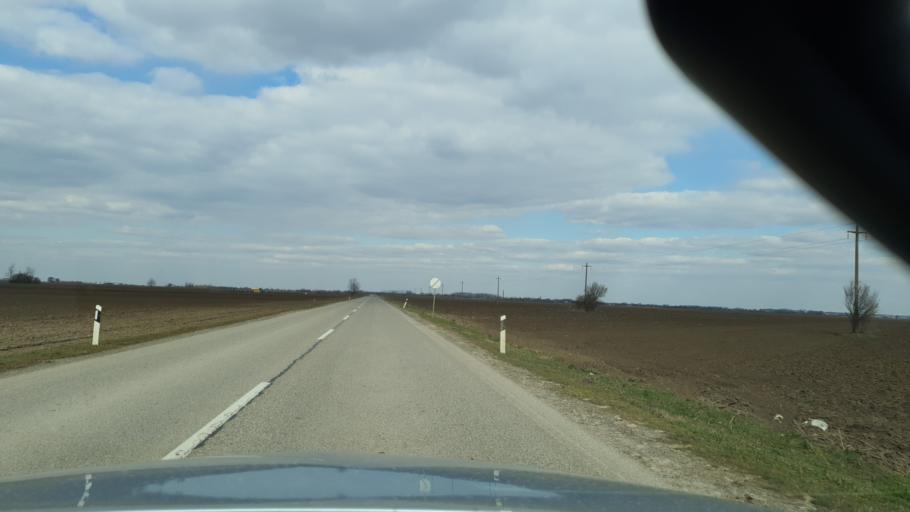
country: RS
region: Autonomna Pokrajina Vojvodina
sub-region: Juznobacki Okrug
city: Bac
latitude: 45.4286
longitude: 19.3072
